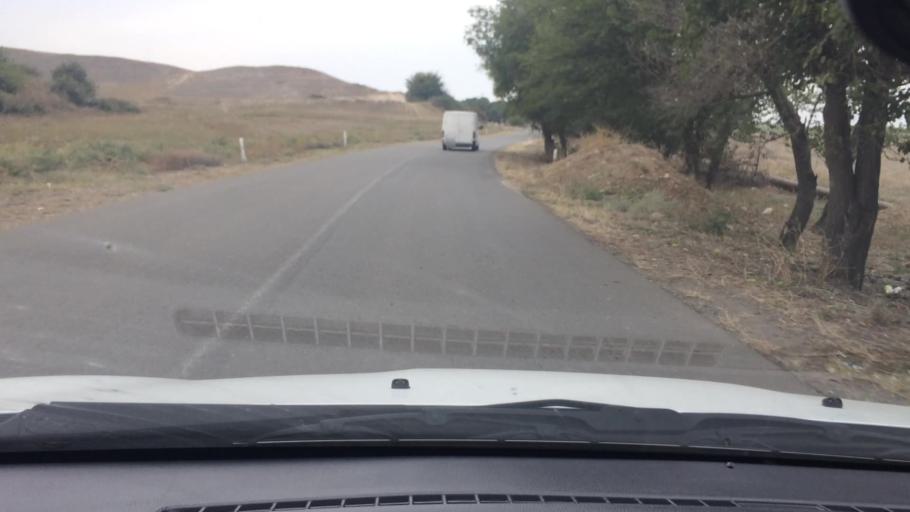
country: AM
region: Tavush
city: Berdavan
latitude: 41.3346
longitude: 45.0313
